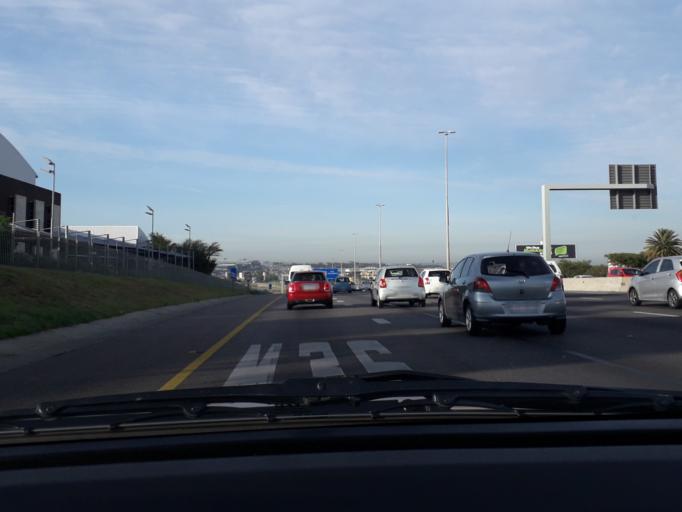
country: ZA
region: Gauteng
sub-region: City of Tshwane Metropolitan Municipality
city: Centurion
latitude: -25.9209
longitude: 28.1502
